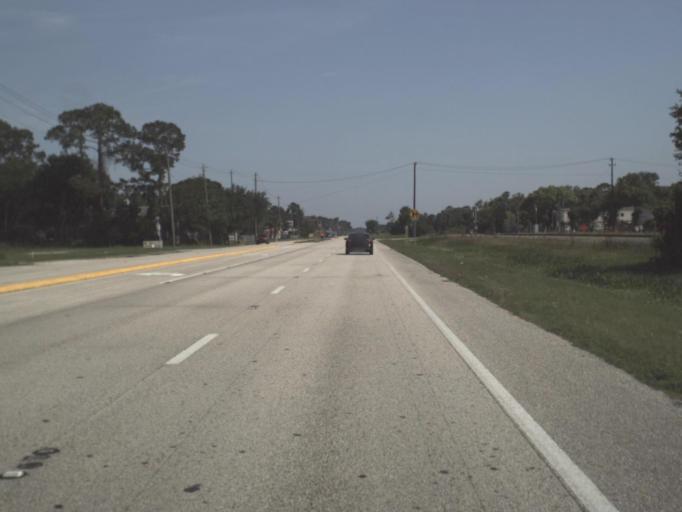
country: US
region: Florida
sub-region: Saint Johns County
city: Villano Beach
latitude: 29.9506
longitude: -81.3414
